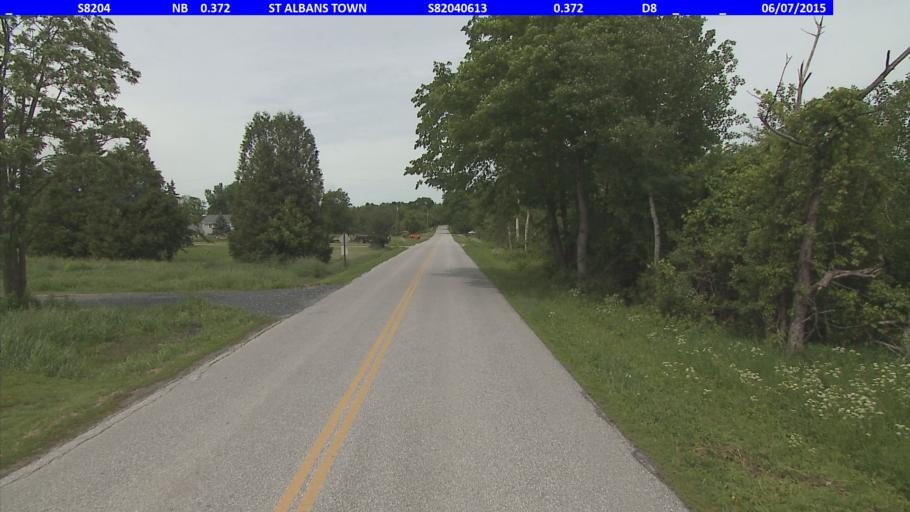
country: US
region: Vermont
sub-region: Franklin County
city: Saint Albans
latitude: 44.8081
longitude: -73.1107
